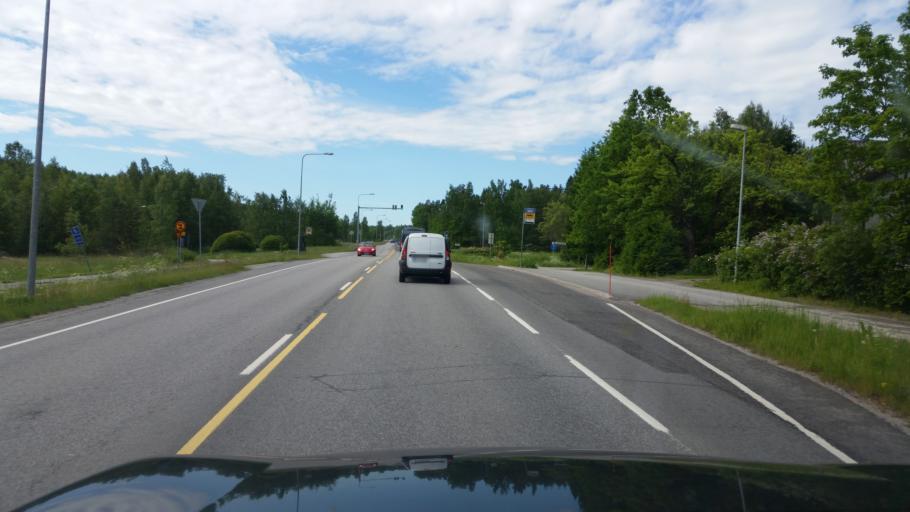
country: FI
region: Varsinais-Suomi
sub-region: Turku
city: Kaarina
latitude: 60.3888
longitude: 22.3916
